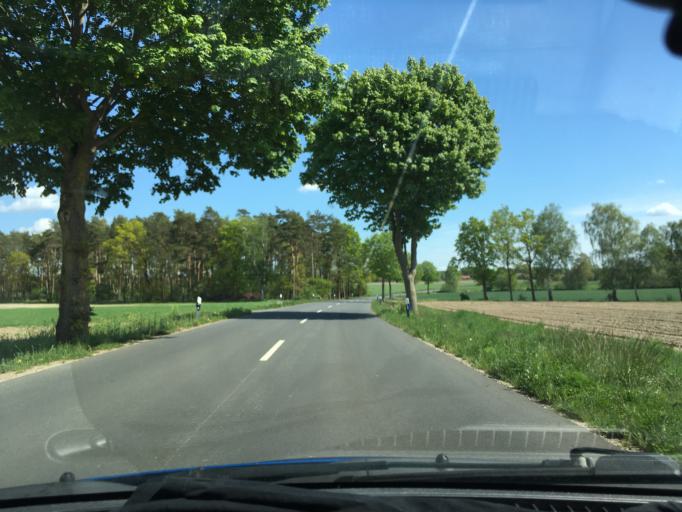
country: DE
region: Lower Saxony
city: Stoetze
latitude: 53.0788
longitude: 10.7585
